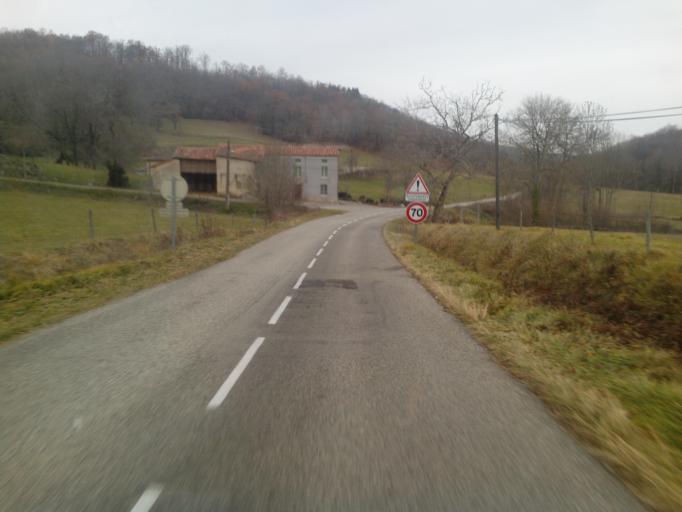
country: FR
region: Midi-Pyrenees
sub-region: Departement de l'Ariege
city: Foix
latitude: 43.0182
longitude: 1.5294
